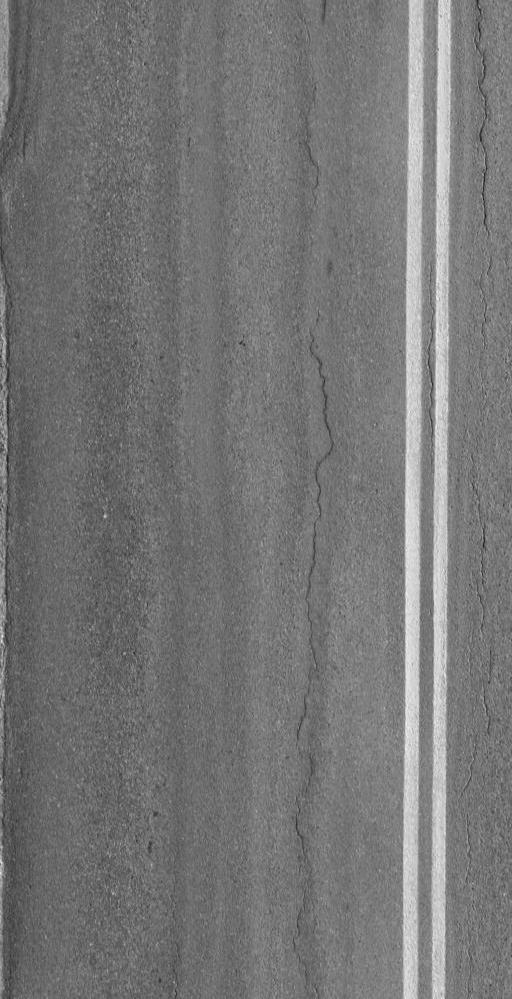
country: US
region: Vermont
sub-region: Chittenden County
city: Hinesburg
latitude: 44.3272
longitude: -73.1909
